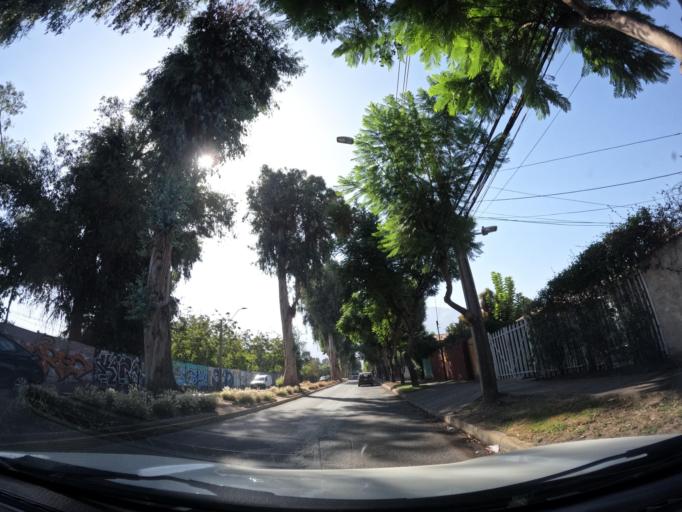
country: CL
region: Santiago Metropolitan
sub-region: Provincia de Santiago
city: Villa Presidente Frei, Nunoa, Santiago, Chile
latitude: -33.5069
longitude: -70.5581
